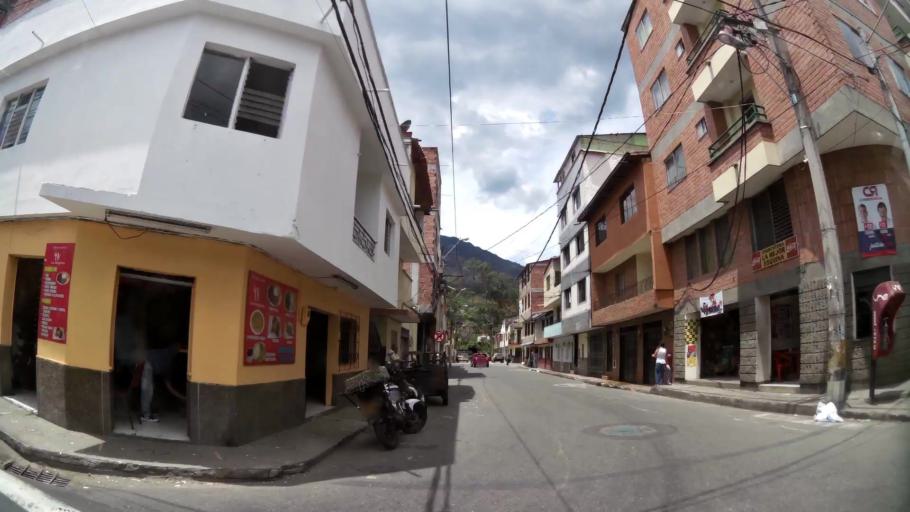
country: CO
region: Antioquia
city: Municipio de Copacabana
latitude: 6.3491
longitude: -75.5063
